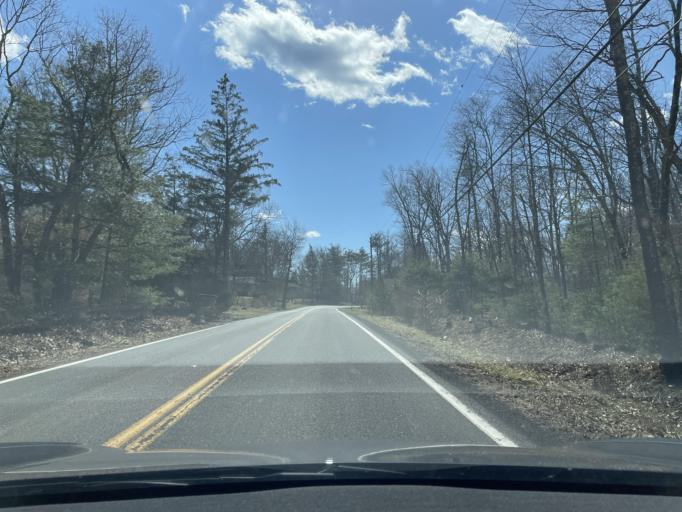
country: US
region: New York
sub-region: Ulster County
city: West Hurley
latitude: 41.9661
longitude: -74.0993
